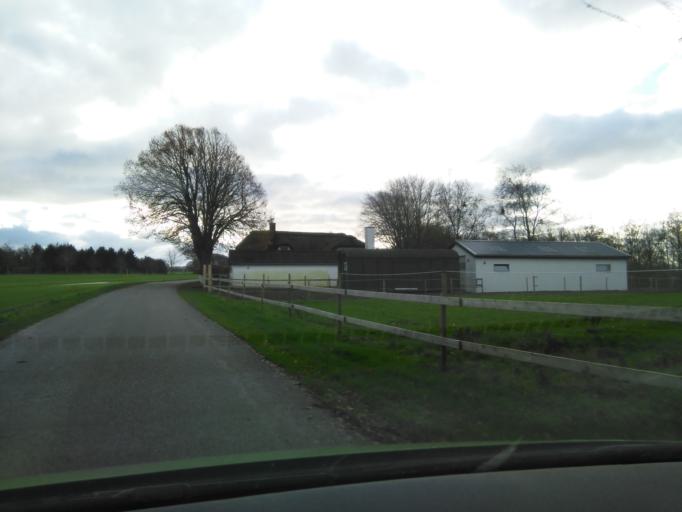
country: DK
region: Central Jutland
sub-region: Odder Kommune
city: Odder
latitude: 55.9263
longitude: 10.1872
